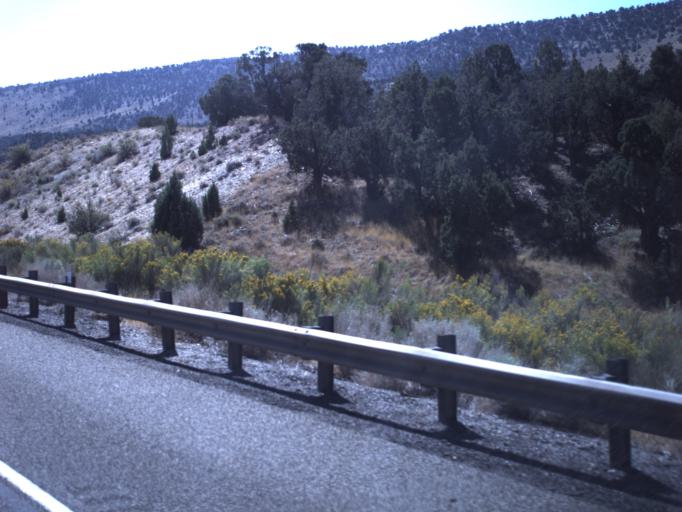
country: US
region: Utah
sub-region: Sevier County
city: Salina
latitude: 38.9288
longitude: -111.7847
